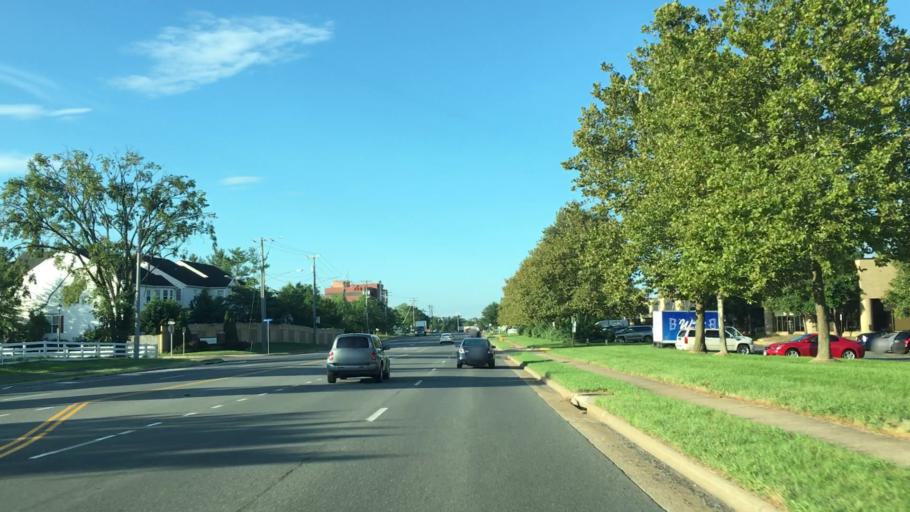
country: US
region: Virginia
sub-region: Fairfax County
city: Chantilly
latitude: 38.8904
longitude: -77.4330
